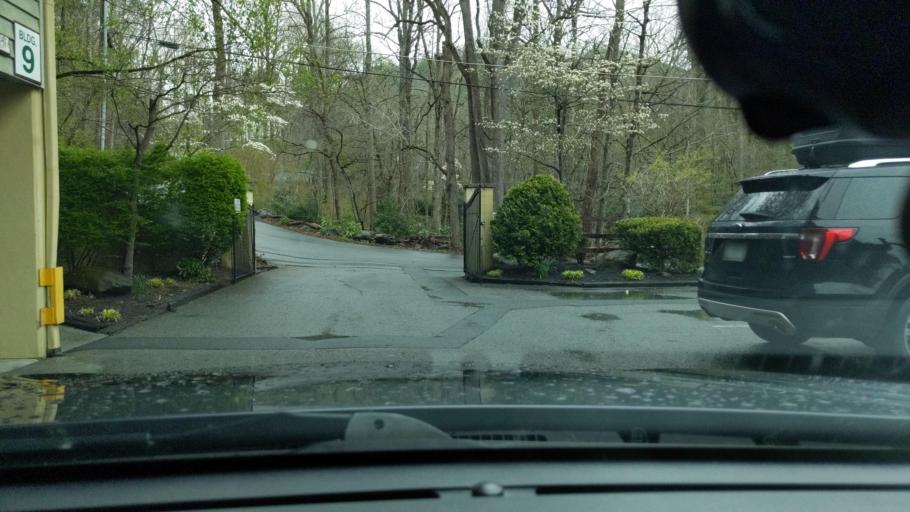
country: US
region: Tennessee
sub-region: Sevier County
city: Gatlinburg
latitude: 35.7172
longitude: -83.4906
